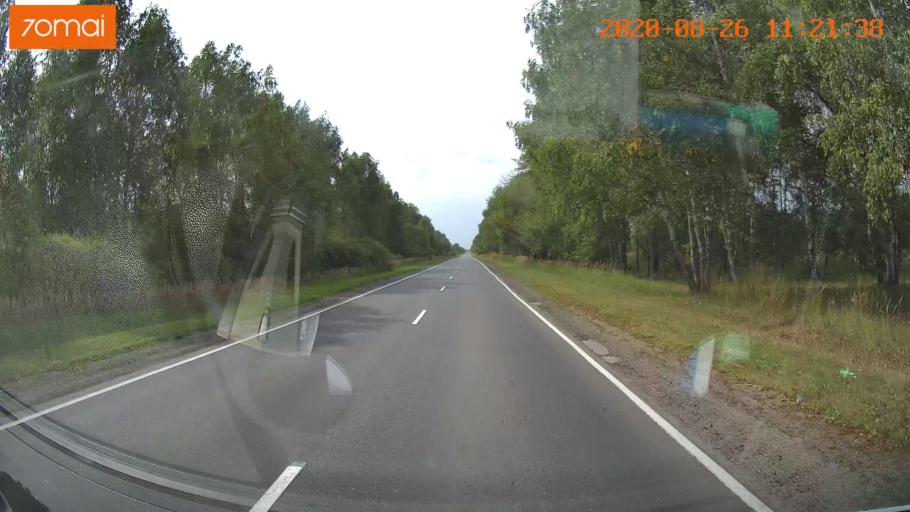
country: RU
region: Rjazan
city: Shilovo
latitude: 54.3738
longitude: 41.0413
